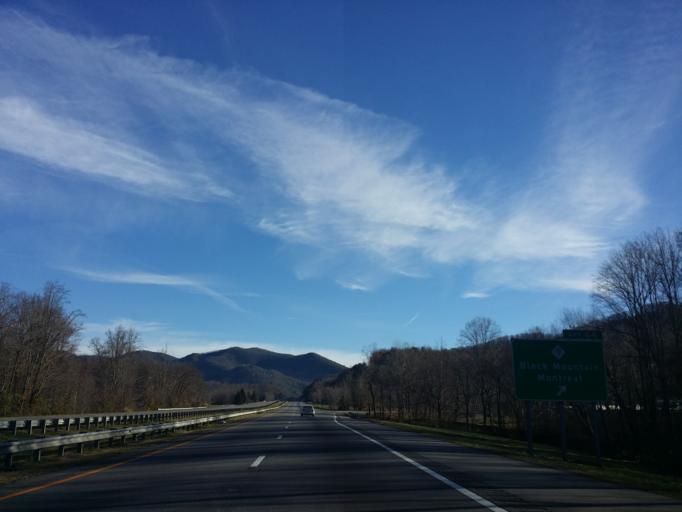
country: US
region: North Carolina
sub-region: Buncombe County
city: Black Mountain
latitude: 35.6090
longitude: -82.3239
